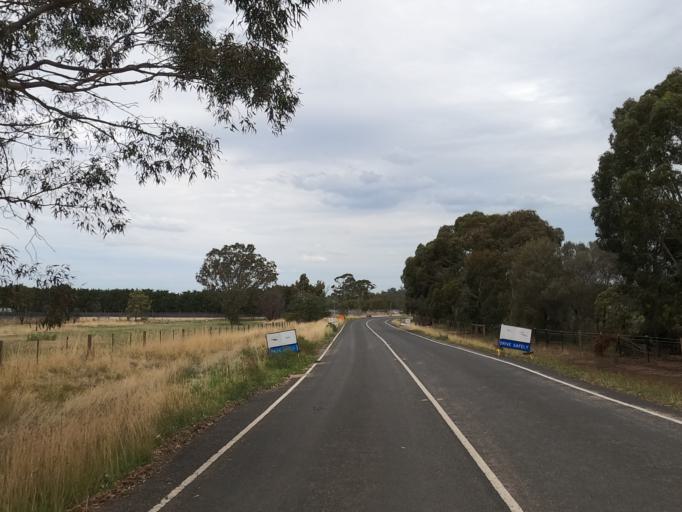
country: AU
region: Victoria
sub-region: Hume
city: Greenvale
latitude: -37.6386
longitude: 144.8712
